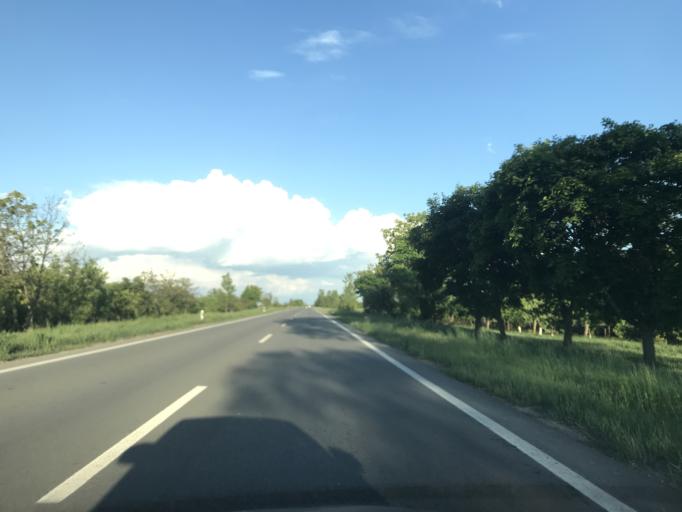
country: RS
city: Aradac
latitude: 45.3895
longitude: 20.3071
